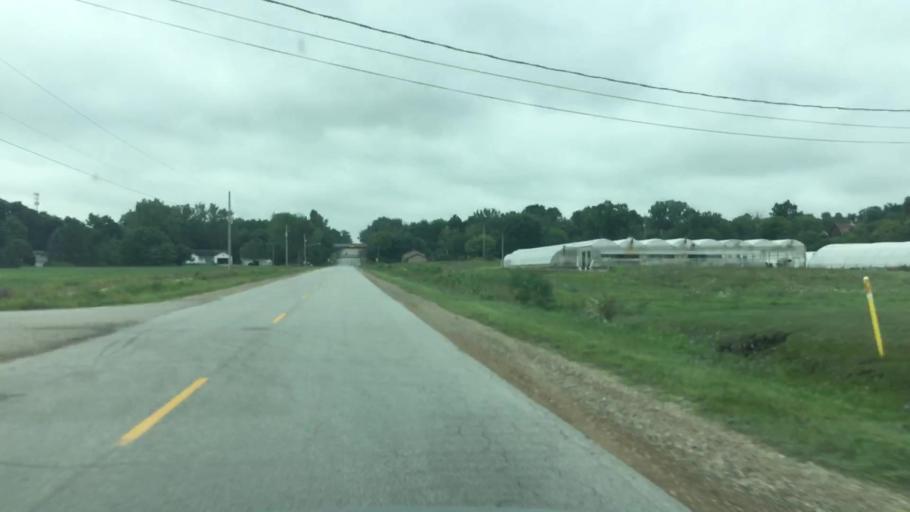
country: US
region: Michigan
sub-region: Ottawa County
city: Hudsonville
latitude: 42.8627
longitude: -85.8364
